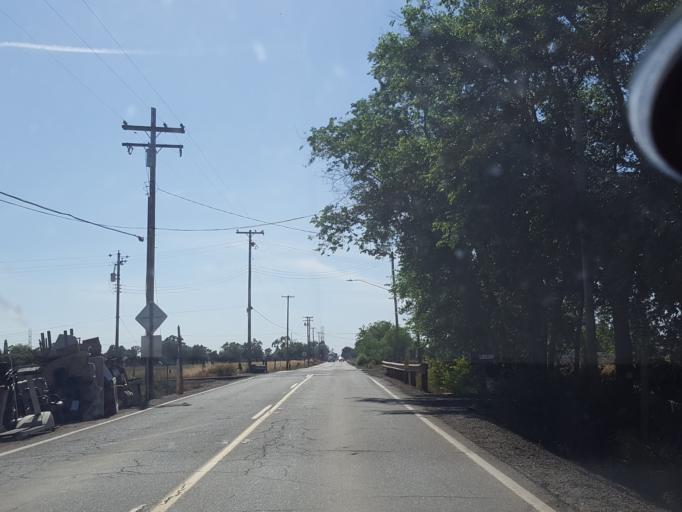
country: US
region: California
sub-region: Sacramento County
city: Vineyard
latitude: 38.4963
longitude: -121.3578
